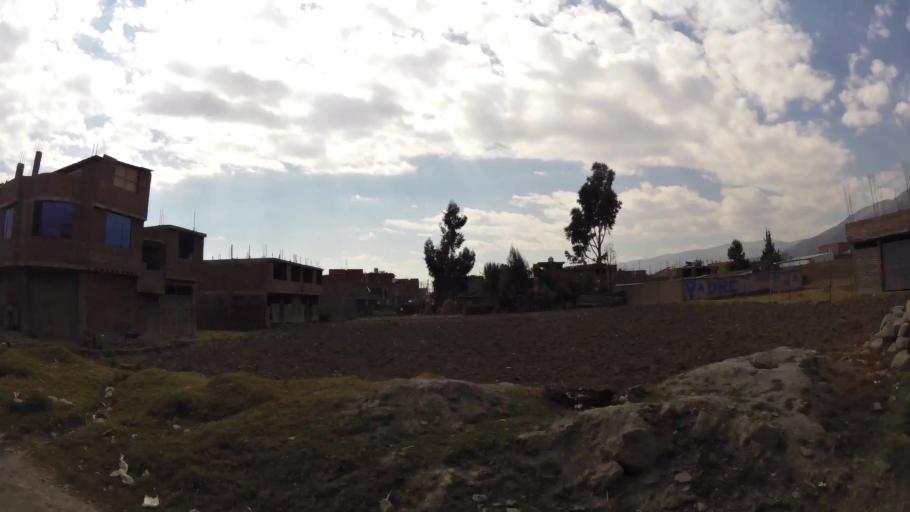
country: PE
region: Junin
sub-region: Provincia de Huancayo
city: Huancayo
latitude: -12.0941
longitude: -75.2040
